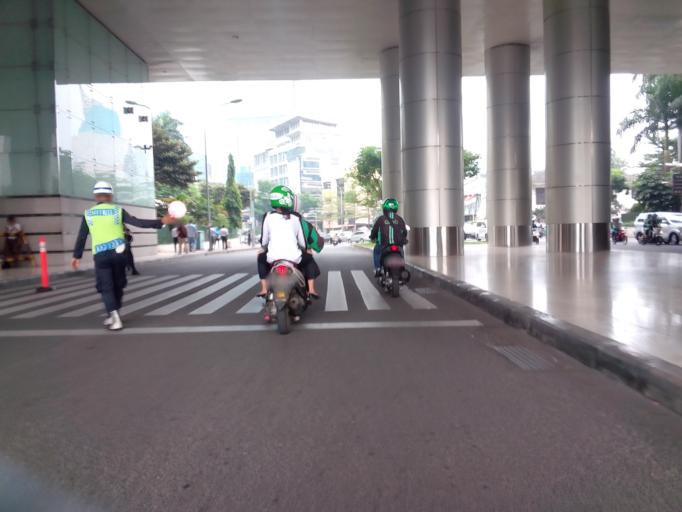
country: ID
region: Jakarta Raya
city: Jakarta
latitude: -6.1949
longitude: 106.8210
